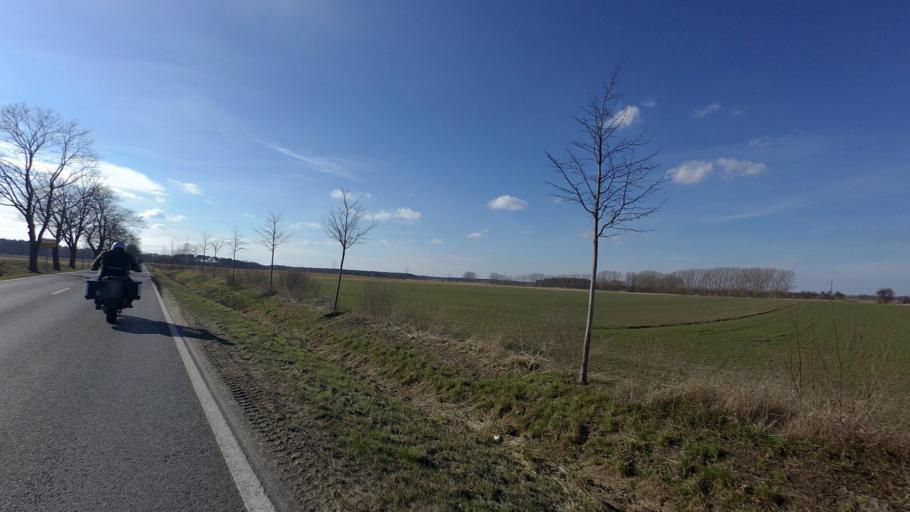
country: DE
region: Brandenburg
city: Wandlitz
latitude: 52.7553
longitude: 13.3683
